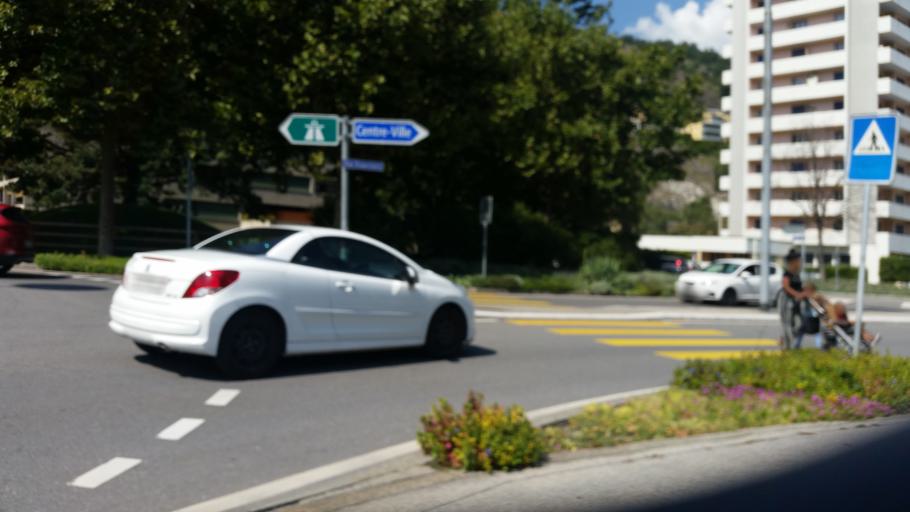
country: CH
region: Valais
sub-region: Sion District
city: Sitten
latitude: 46.2276
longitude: 7.3465
